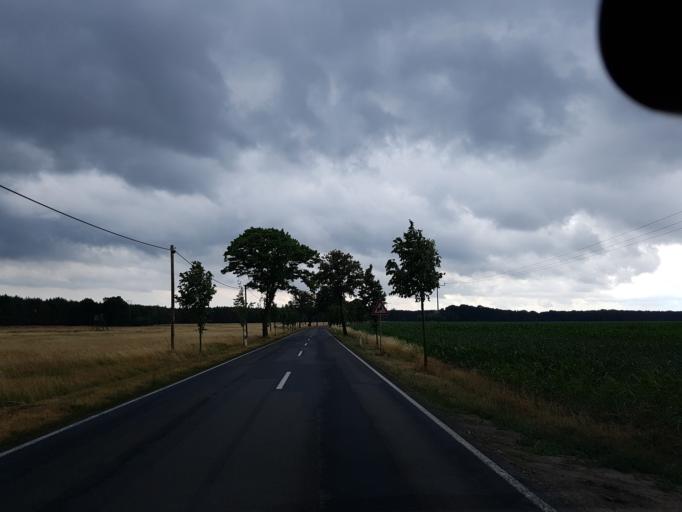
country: DE
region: Saxony-Anhalt
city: Seyda
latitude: 51.9014
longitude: 12.9384
